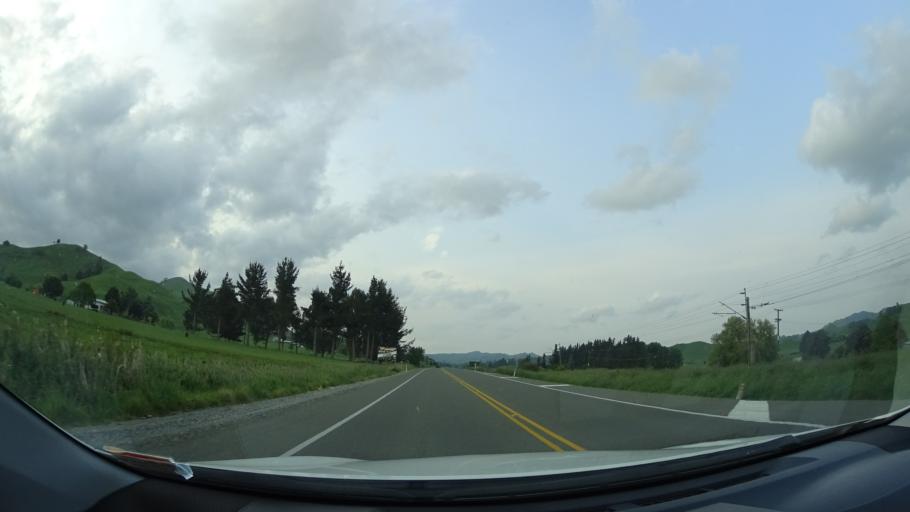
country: NZ
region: Manawatu-Wanganui
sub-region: Ruapehu District
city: Waiouru
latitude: -39.7276
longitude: 175.8428
